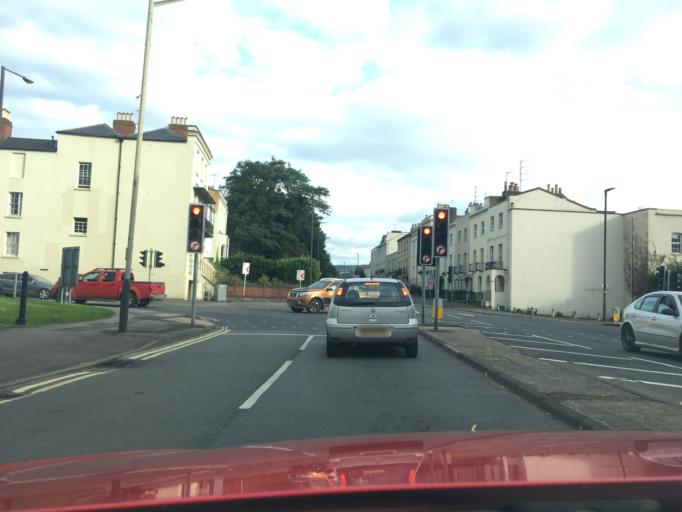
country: GB
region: England
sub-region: Gloucestershire
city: Cheltenham
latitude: 51.8940
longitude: -2.0647
